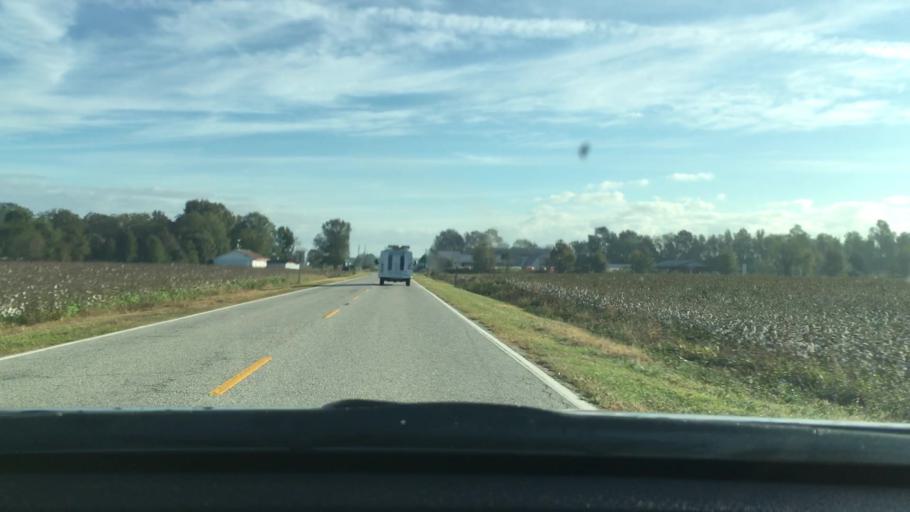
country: US
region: South Carolina
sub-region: Lee County
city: Bishopville
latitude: 34.0650
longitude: -80.2206
